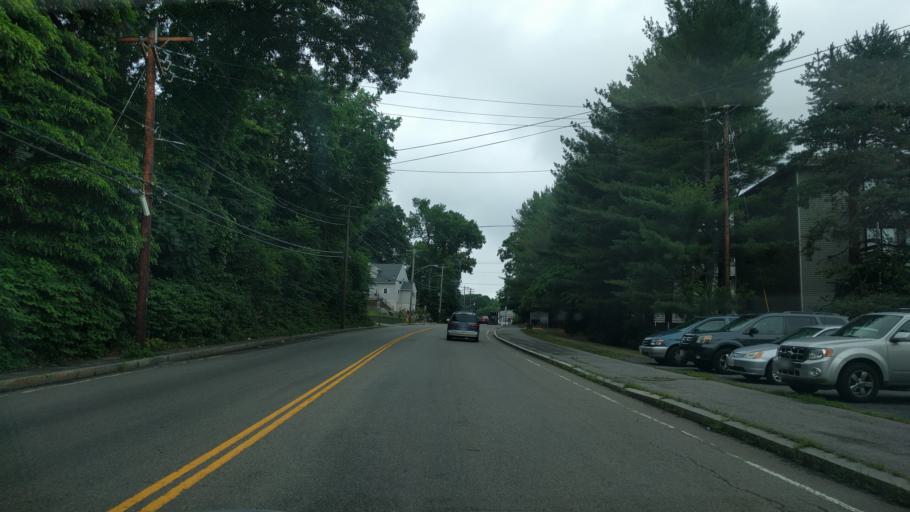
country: US
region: Massachusetts
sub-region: Worcester County
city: Sunderland
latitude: 42.2385
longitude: -71.7529
